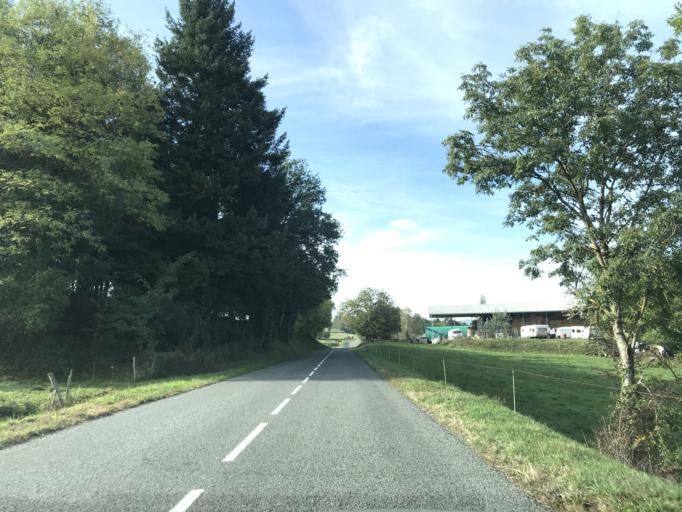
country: FR
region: Rhone-Alpes
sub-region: Departement de la Savoie
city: Yenne
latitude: 45.6837
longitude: 5.7949
